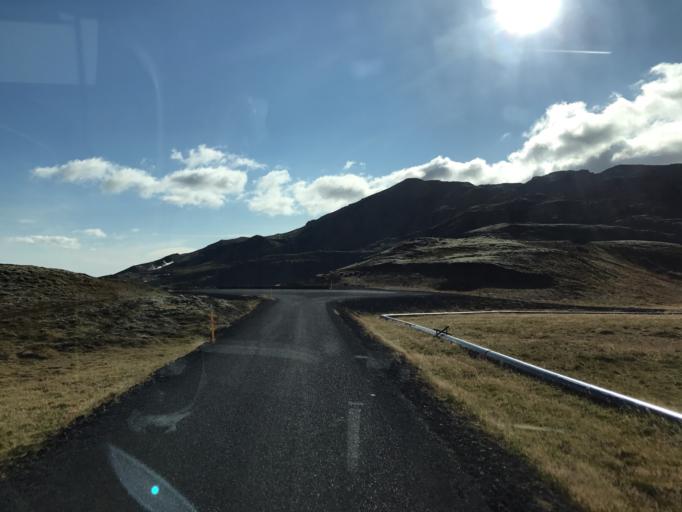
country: IS
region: South
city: Hveragerdi
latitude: 64.1045
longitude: -21.2767
